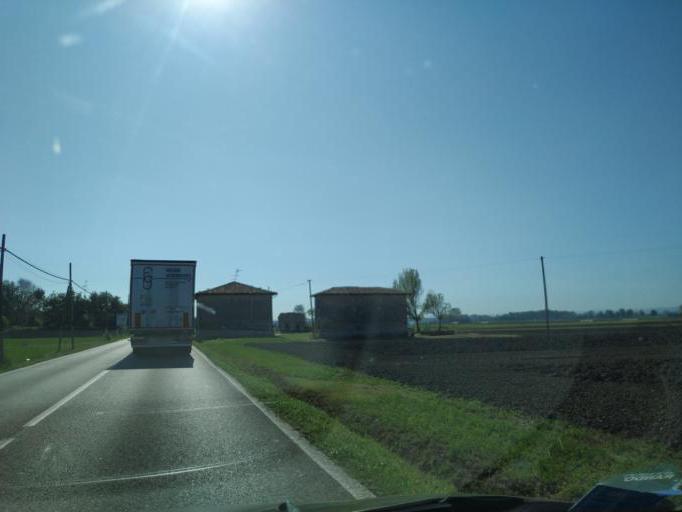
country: IT
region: Emilia-Romagna
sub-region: Provincia di Bologna
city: Sant'Agata Bolognese
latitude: 44.6526
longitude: 11.1482
